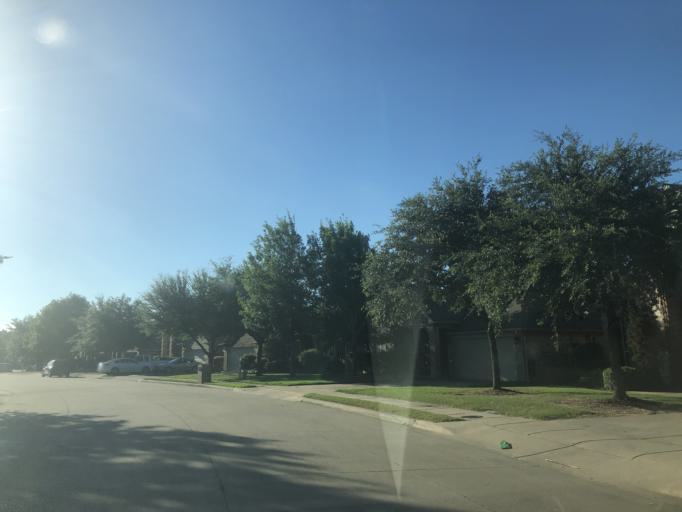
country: US
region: Texas
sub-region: Dallas County
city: Duncanville
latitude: 32.6574
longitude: -96.9518
